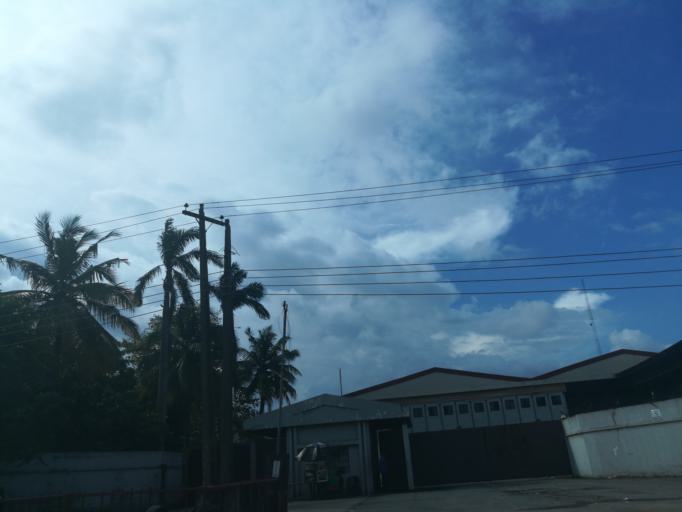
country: NG
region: Lagos
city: Agege
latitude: 6.6260
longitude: 3.3459
